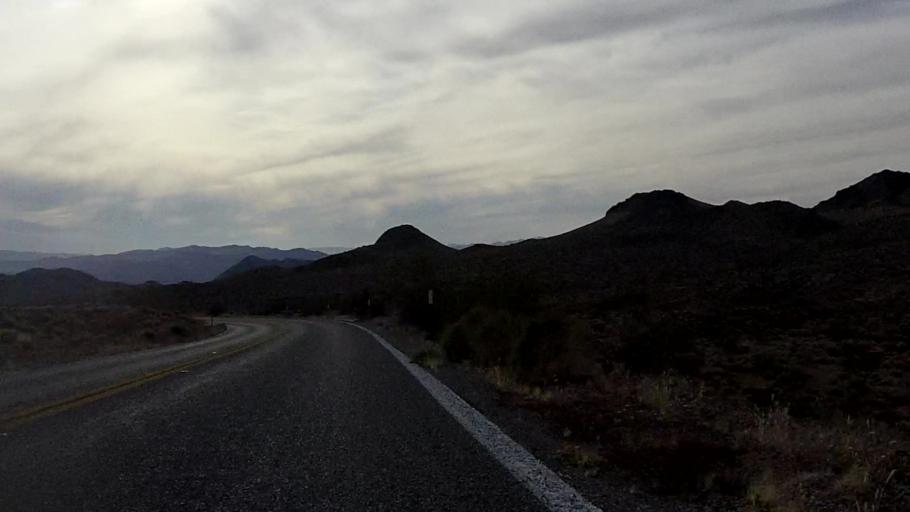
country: US
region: Nevada
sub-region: Nye County
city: Pahrump
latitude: 35.9234
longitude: -116.4329
